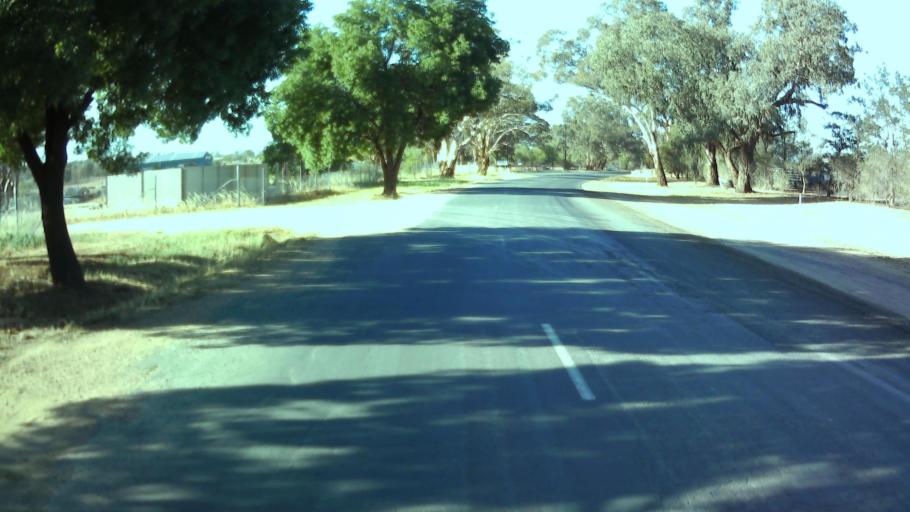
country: AU
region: New South Wales
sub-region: Weddin
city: Grenfell
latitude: -33.9004
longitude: 148.1522
